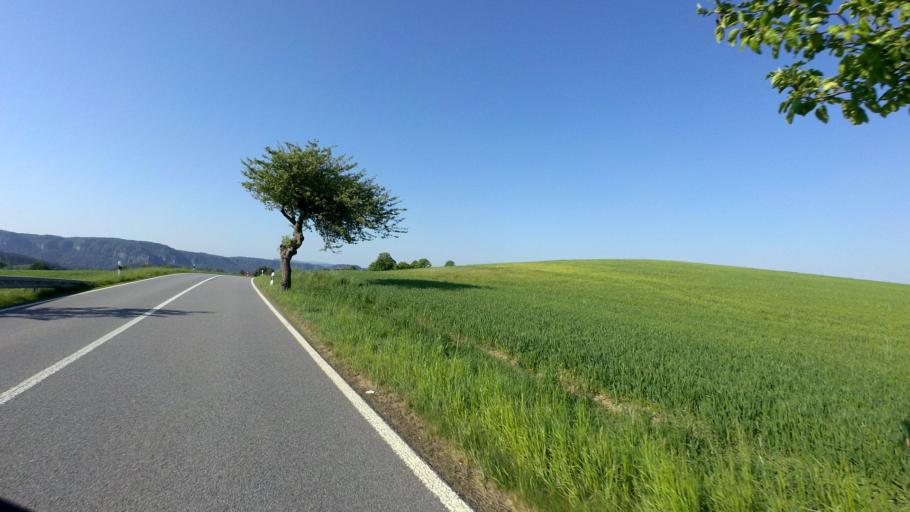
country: DE
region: Saxony
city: Sebnitz
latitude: 50.9492
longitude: 14.2450
